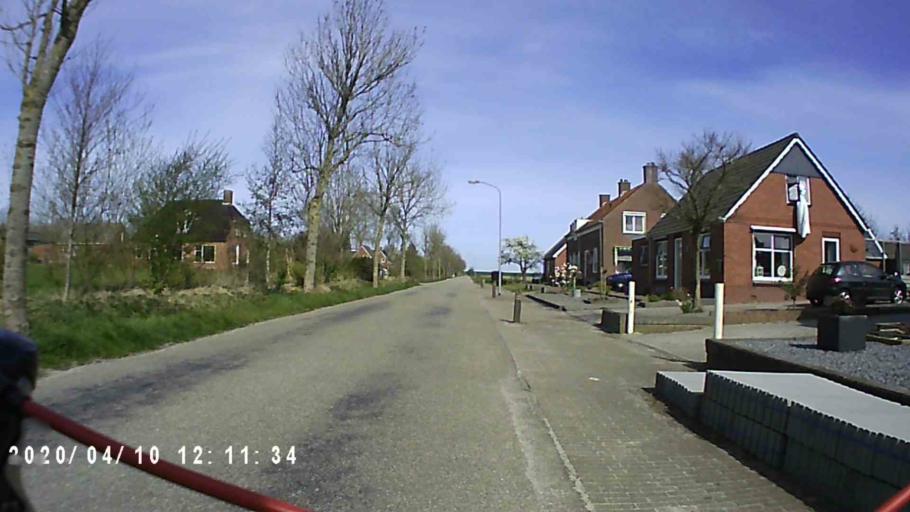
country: NL
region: Groningen
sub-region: Gemeente De Marne
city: Ulrum
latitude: 53.3895
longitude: 6.3743
